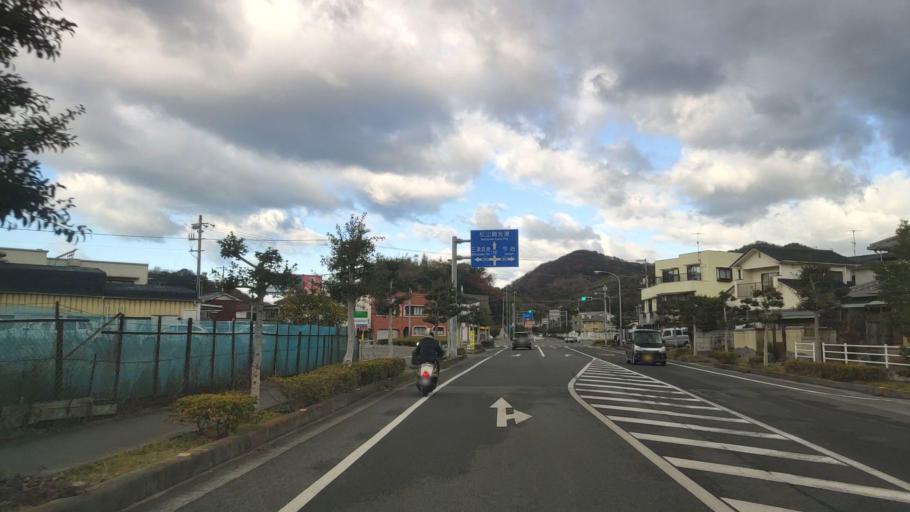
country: JP
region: Ehime
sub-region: Shikoku-chuo Shi
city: Matsuyama
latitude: 33.8713
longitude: 132.7206
